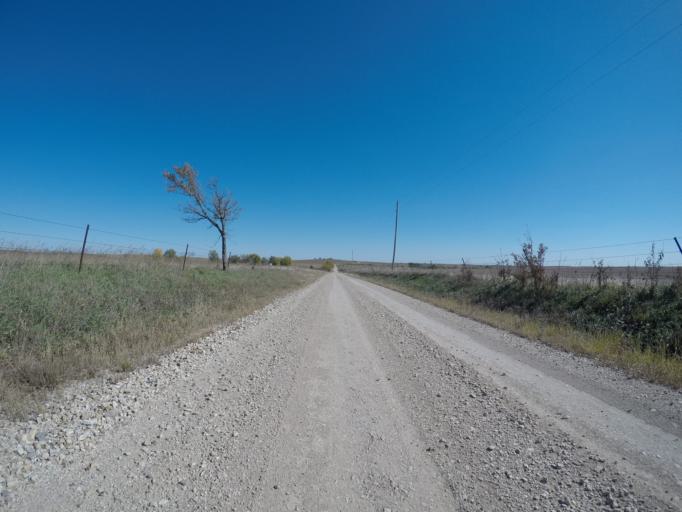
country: US
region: Kansas
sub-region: Wabaunsee County
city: Alma
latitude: 39.0434
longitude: -96.3626
